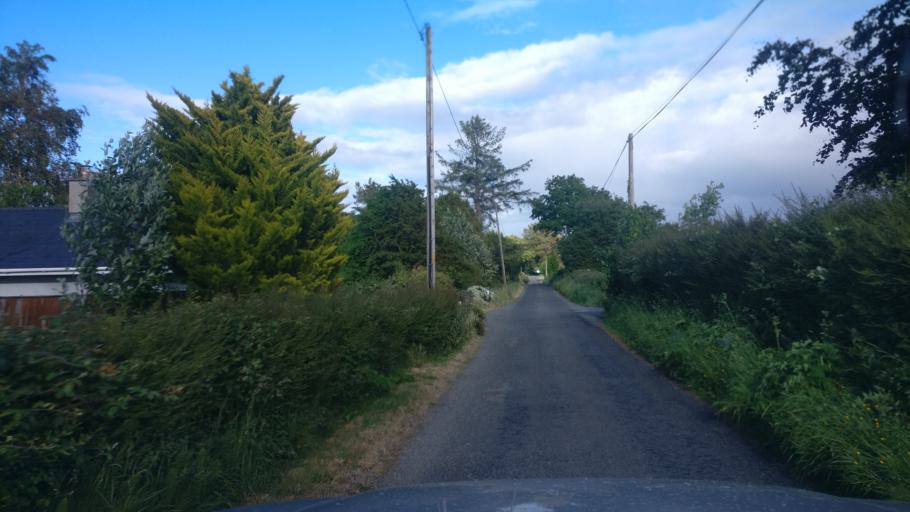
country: IE
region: Connaught
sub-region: County Galway
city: Ballinasloe
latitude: 53.2452
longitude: -8.2075
